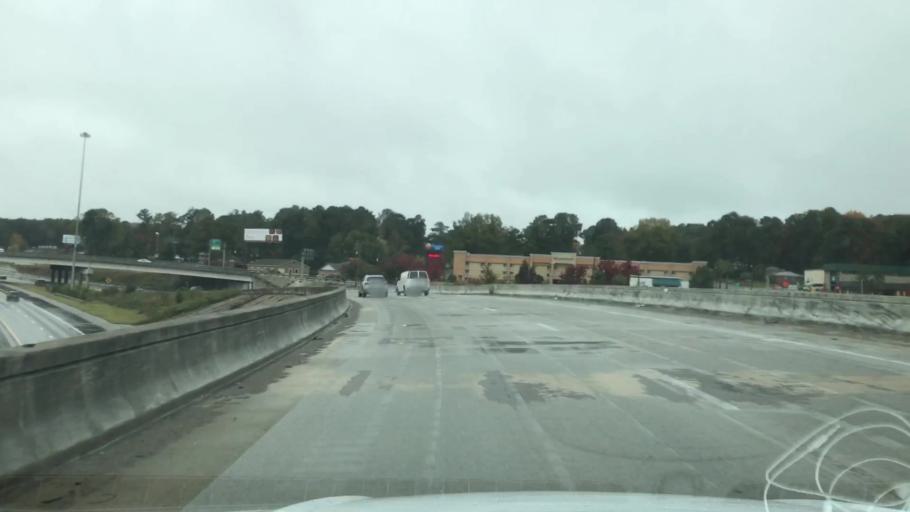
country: US
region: South Carolina
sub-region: Lexington County
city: Saint Andrews
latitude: 34.0283
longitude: -81.1017
